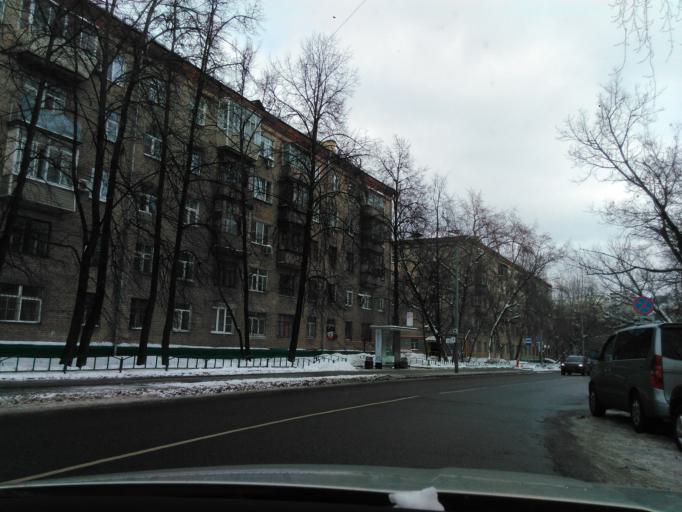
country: RU
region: Moskovskaya
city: Dorogomilovo
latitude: 55.7998
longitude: 37.5667
